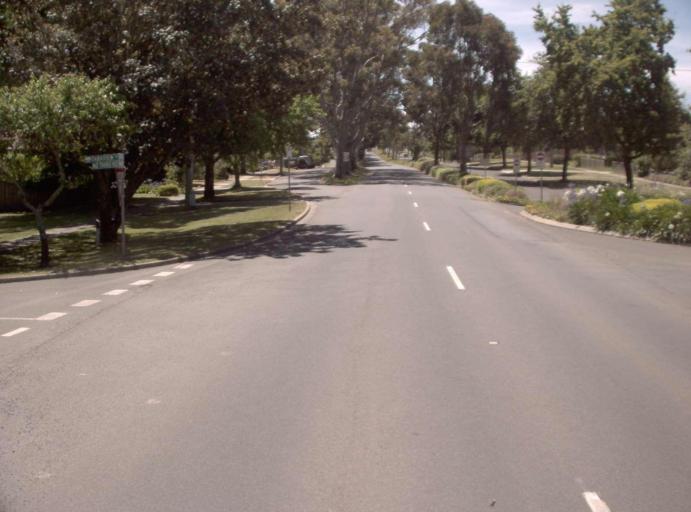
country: AU
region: Victoria
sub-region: Baw Baw
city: Warragul
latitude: -38.0148
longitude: 145.9550
